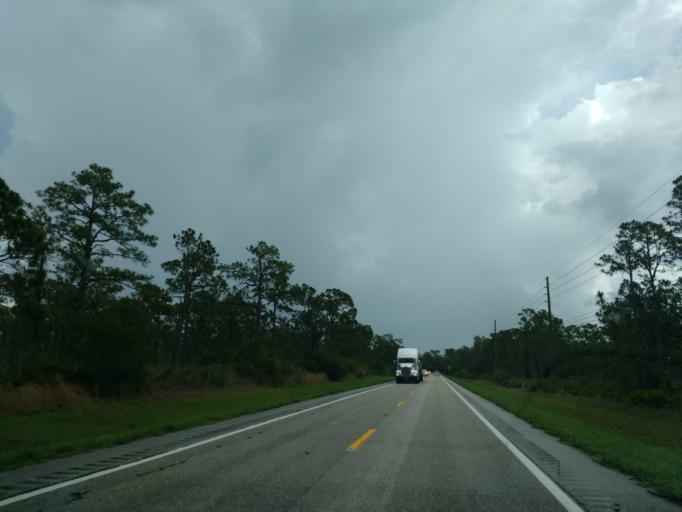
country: US
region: Florida
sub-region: Lee County
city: Burnt Store Marina
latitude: 26.8115
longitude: -82.0247
